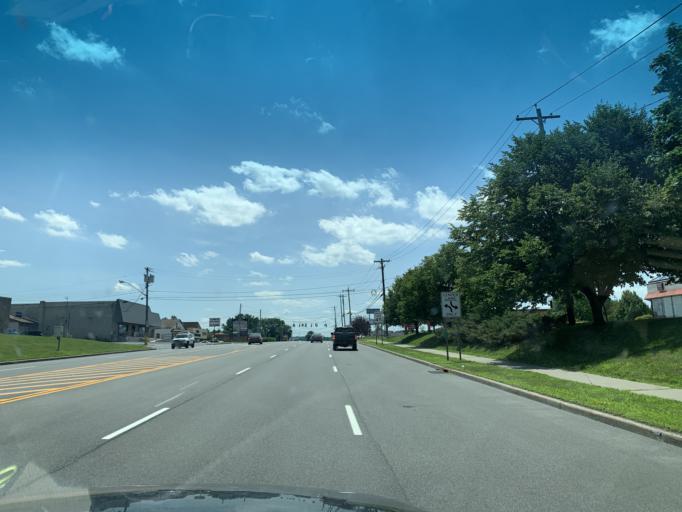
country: US
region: New York
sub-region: Oneida County
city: New York Mills
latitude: 43.0899
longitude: -75.3109
